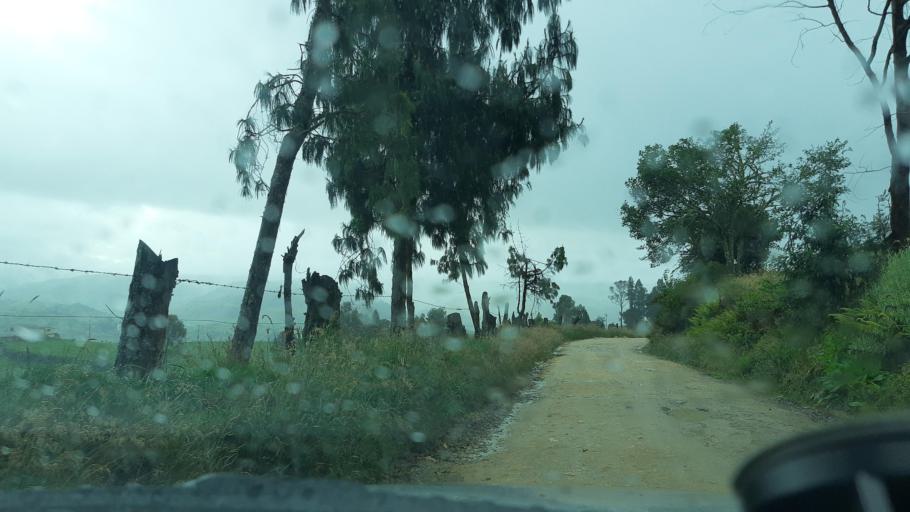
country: CO
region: Cundinamarca
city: Villapinzon
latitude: 5.2101
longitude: -73.5686
